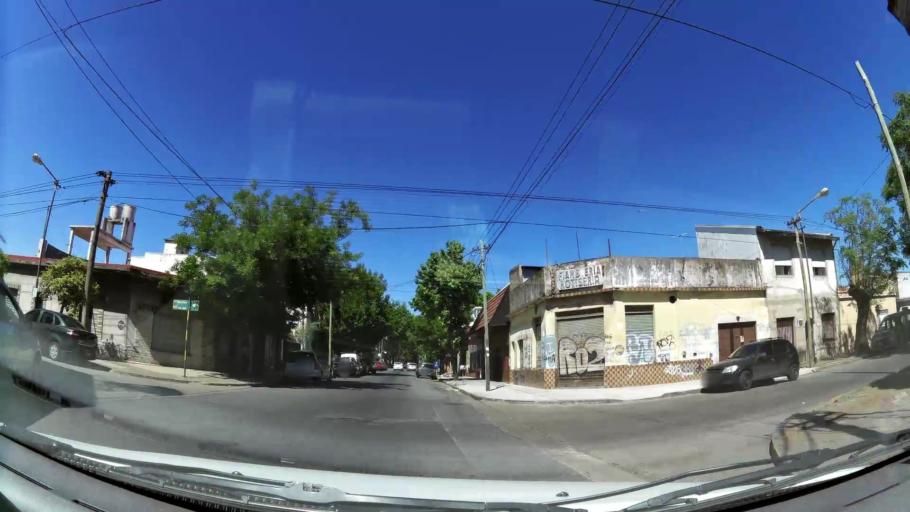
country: AR
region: Buenos Aires
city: Caseros
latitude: -34.5849
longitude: -58.5480
